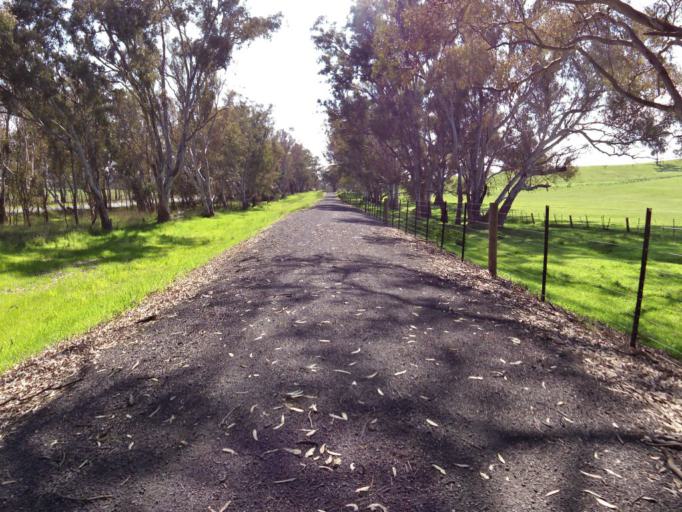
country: AU
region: Victoria
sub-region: Murrindindi
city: Alexandra
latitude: -37.1388
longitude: 145.5906
